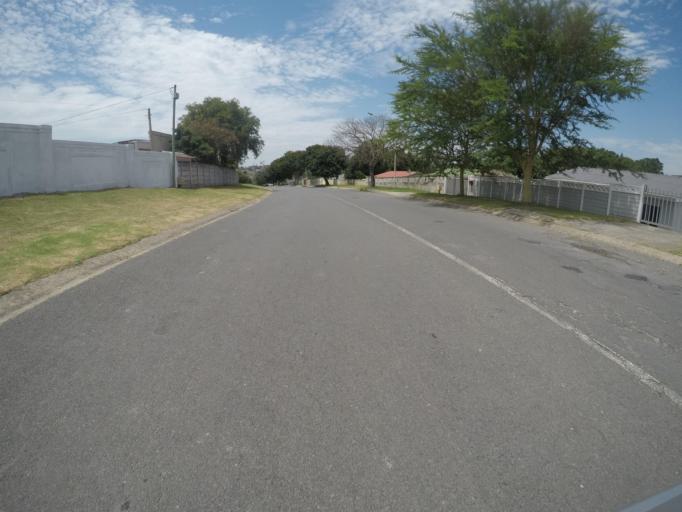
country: ZA
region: Eastern Cape
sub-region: Buffalo City Metropolitan Municipality
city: East London
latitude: -32.9800
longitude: 27.8641
